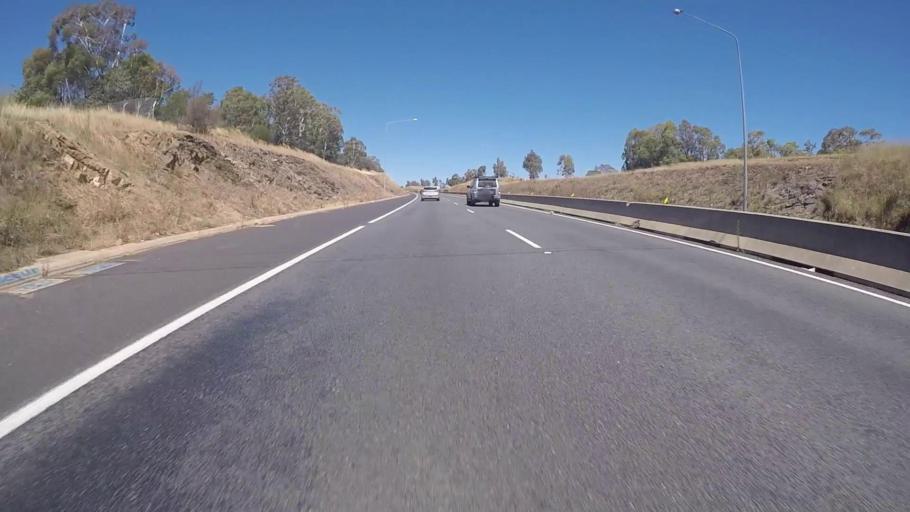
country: AU
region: Australian Capital Territory
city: Forrest
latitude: -35.3278
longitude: 149.0638
